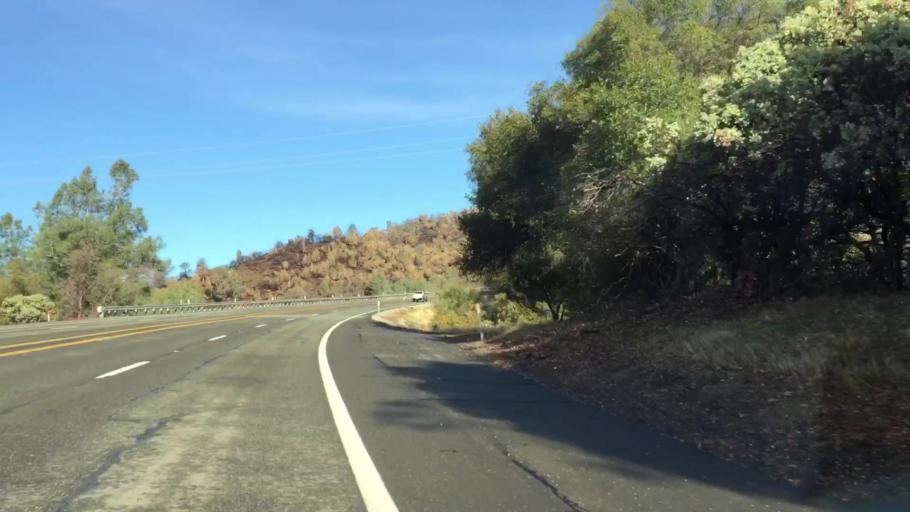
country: US
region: California
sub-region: Butte County
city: Paradise
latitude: 39.6817
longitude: -121.5461
